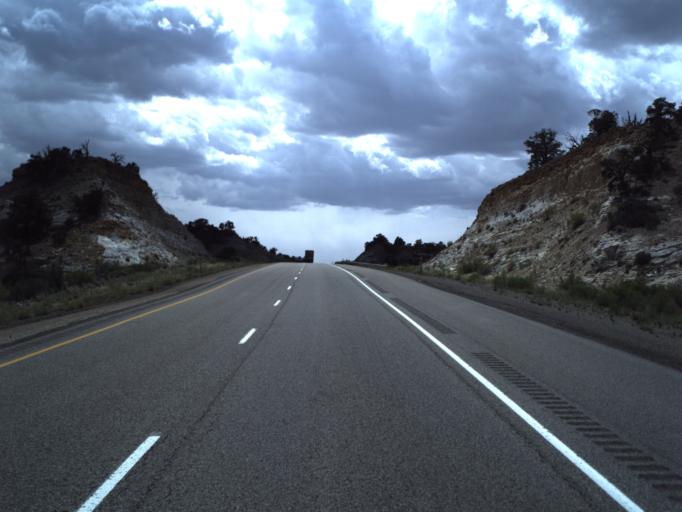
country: US
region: Utah
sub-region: Emery County
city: Ferron
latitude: 38.8512
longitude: -110.8837
